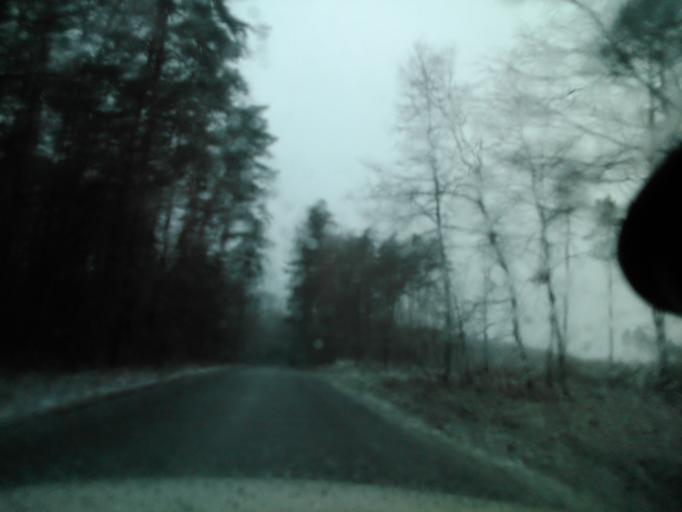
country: PL
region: Warmian-Masurian Voivodeship
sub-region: Powiat dzialdowski
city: Rybno
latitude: 53.3296
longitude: 19.9319
